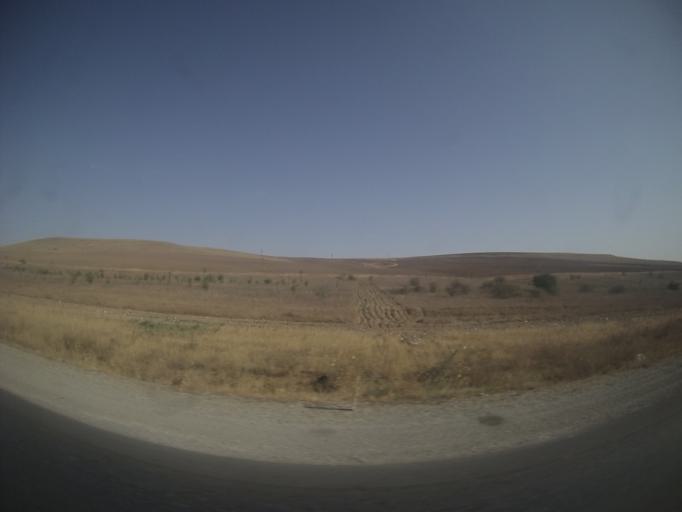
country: AZ
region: Qobustan
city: Qobustan
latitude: 40.5239
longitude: 48.8619
